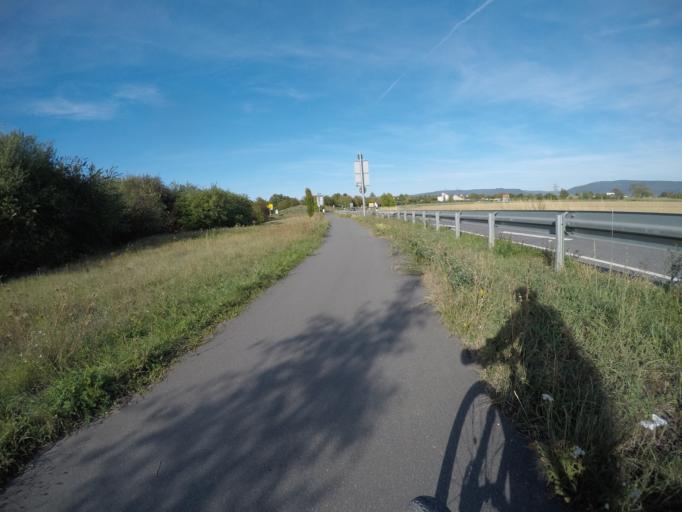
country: DE
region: Baden-Wuerttemberg
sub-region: Karlsruhe Region
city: Plankstadt
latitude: 49.3857
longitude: 8.5972
